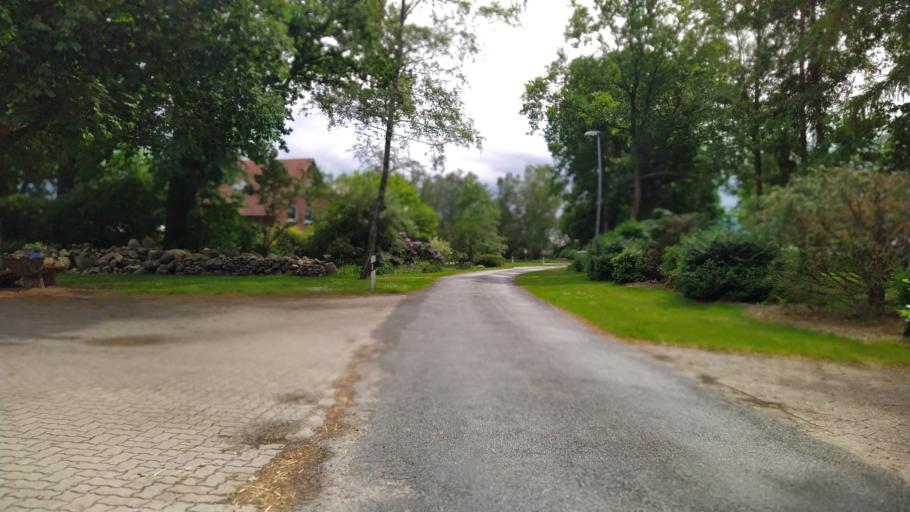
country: DE
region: Lower Saxony
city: Farven
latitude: 53.4473
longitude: 9.3204
